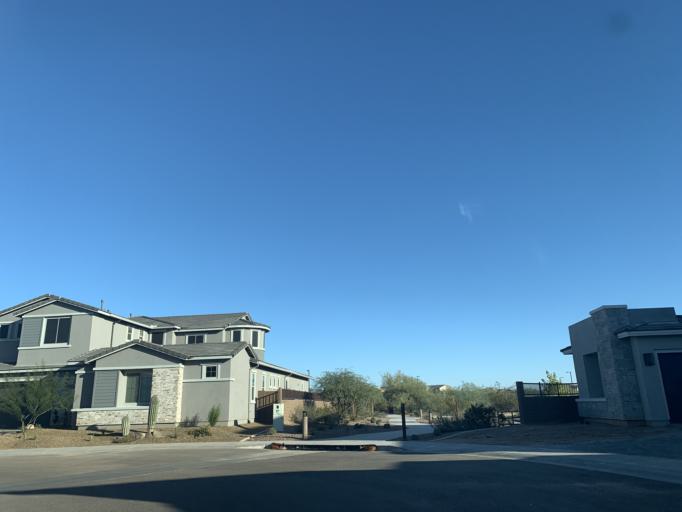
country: US
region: Arizona
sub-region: Maricopa County
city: Cave Creek
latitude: 33.6873
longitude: -112.0163
